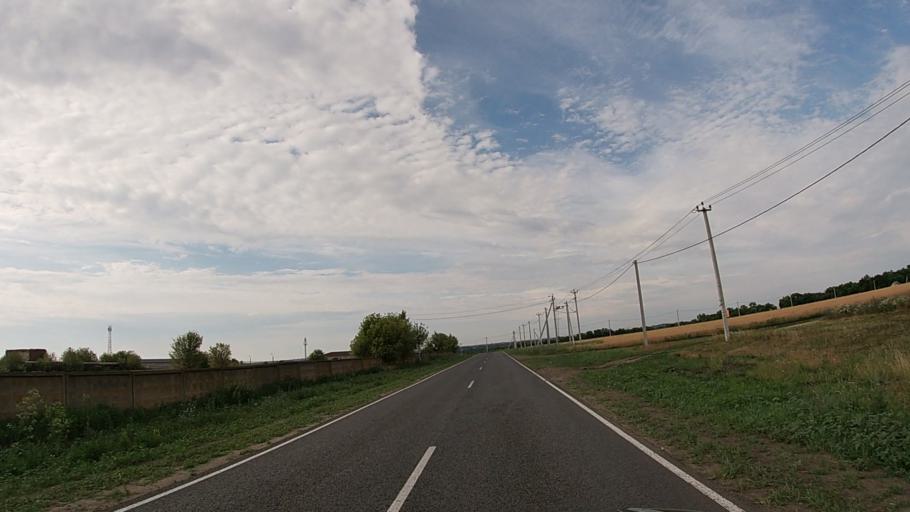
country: RU
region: Belgorod
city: Severnyy
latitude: 50.7235
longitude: 36.5845
